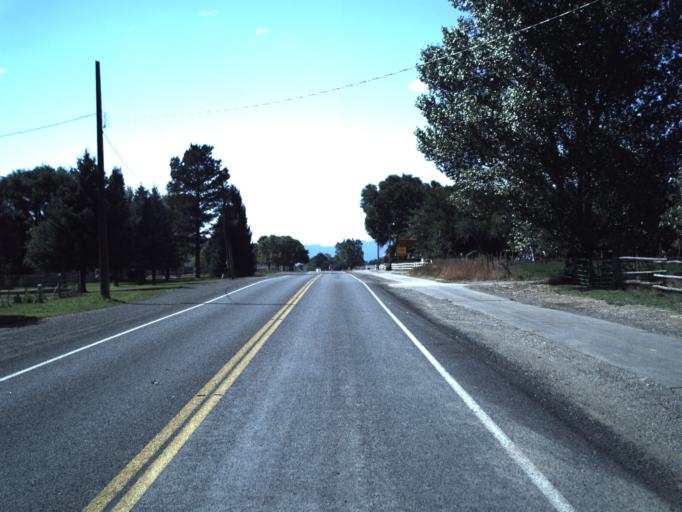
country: US
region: Utah
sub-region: Beaver County
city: Beaver
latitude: 38.2769
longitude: -112.6137
